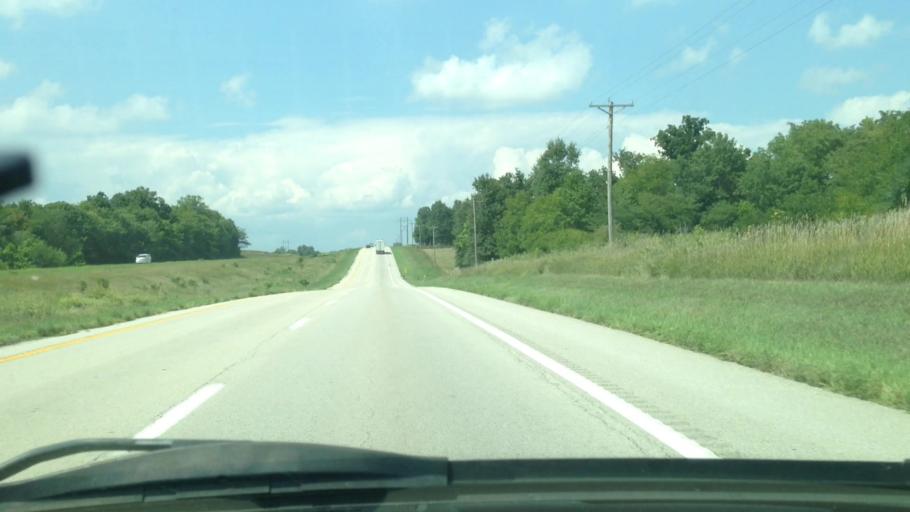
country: US
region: Missouri
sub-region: Lincoln County
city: Troy
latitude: 39.1445
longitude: -90.9674
